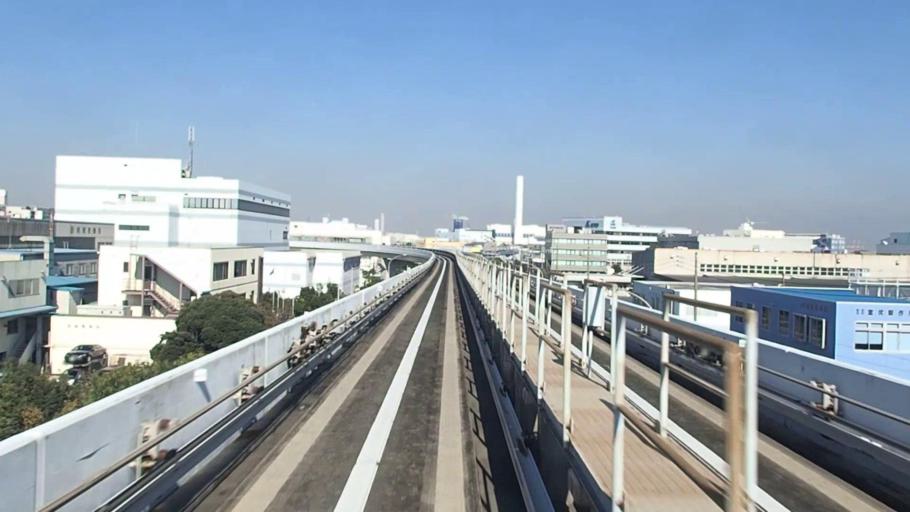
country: JP
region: Kanagawa
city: Yokosuka
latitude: 35.3514
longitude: 139.6485
